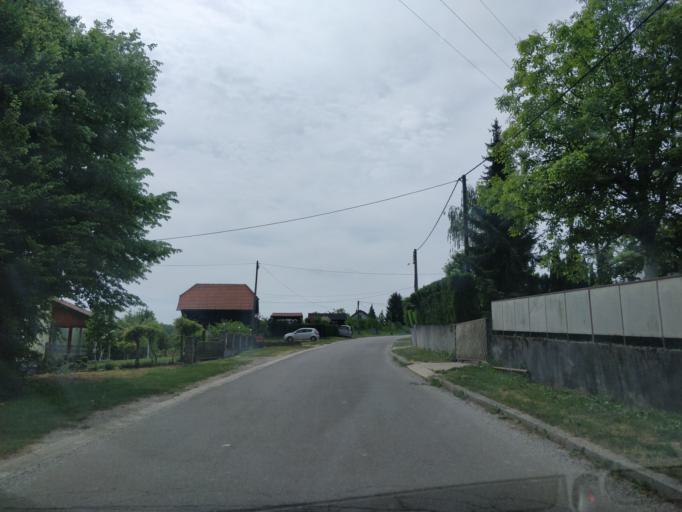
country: HR
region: Zagrebacka
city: Mraclin
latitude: 45.6279
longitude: 16.0428
